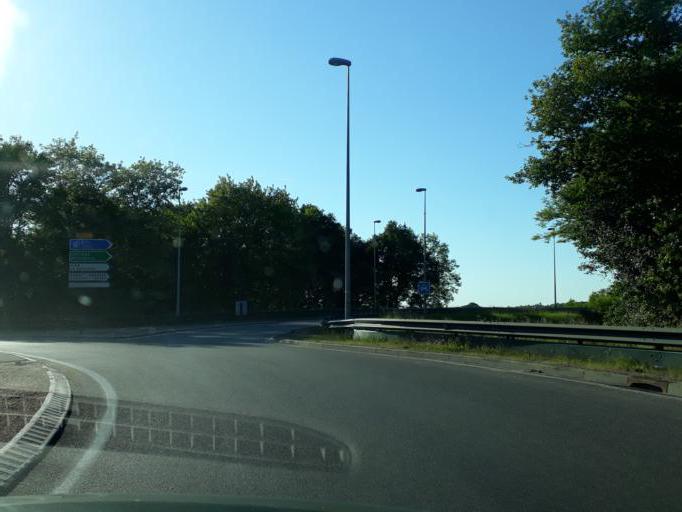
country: FR
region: Centre
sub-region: Departement du Loiret
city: Briare
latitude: 47.6232
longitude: 2.7582
